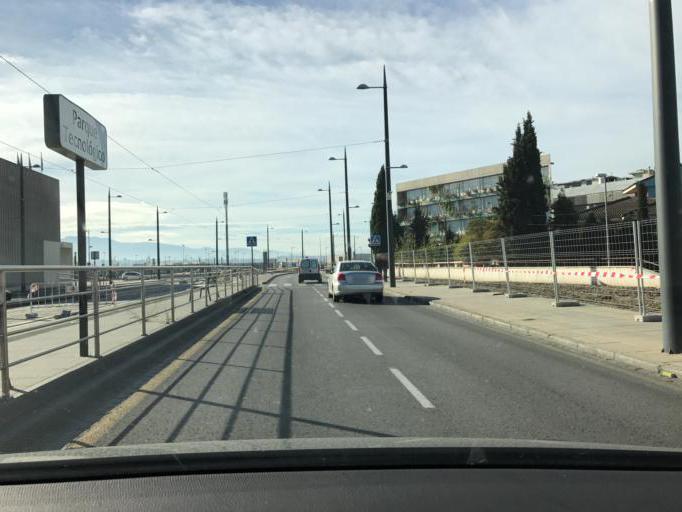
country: ES
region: Andalusia
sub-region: Provincia de Granada
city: Armilla
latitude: 37.1490
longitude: -3.6070
